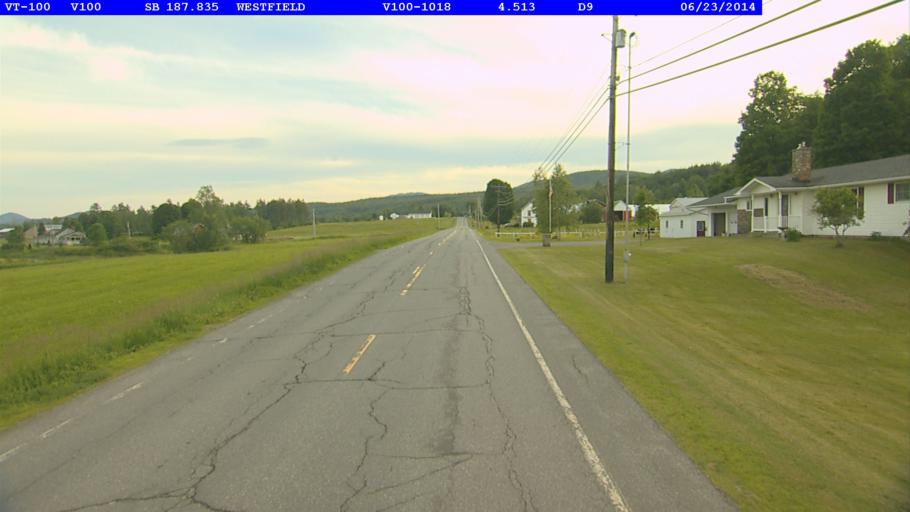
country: US
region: Vermont
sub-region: Orleans County
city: Newport
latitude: 44.8951
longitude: -72.4168
